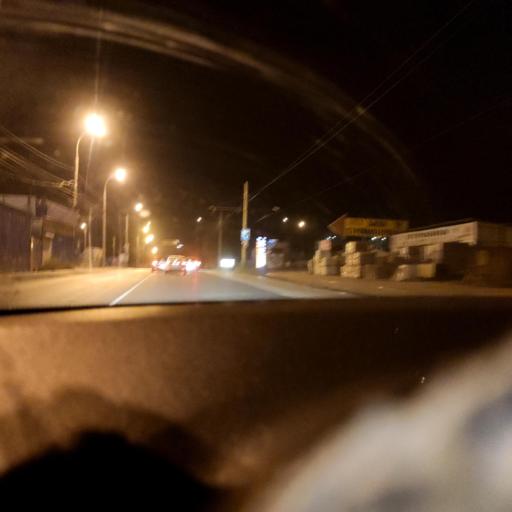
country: RU
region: Samara
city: Petra-Dubrava
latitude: 53.2269
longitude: 50.2806
